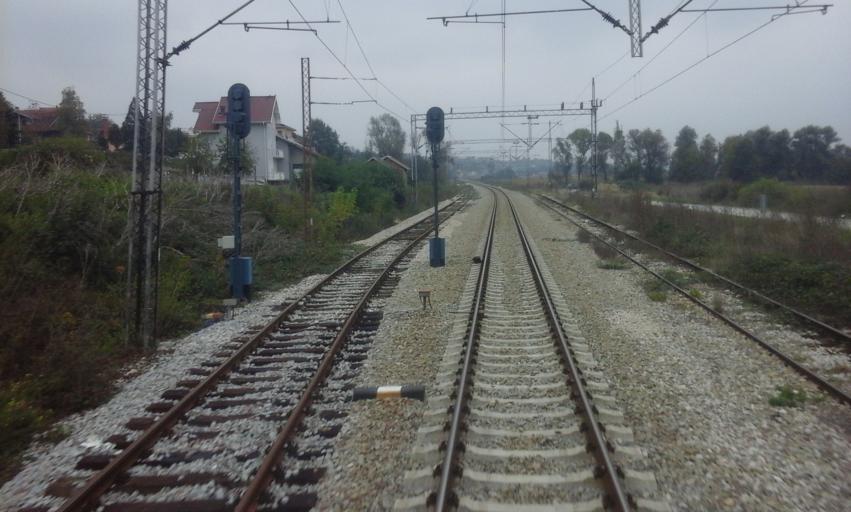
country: RS
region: Central Serbia
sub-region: Belgrade
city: Mladenovac
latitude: 44.4842
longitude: 20.6576
